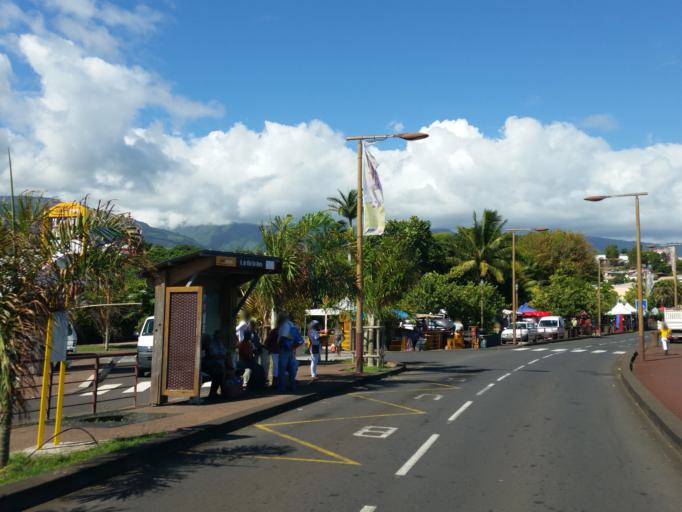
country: RE
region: Reunion
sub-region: Reunion
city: Sainte-Marie
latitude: -20.8959
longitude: 55.5507
